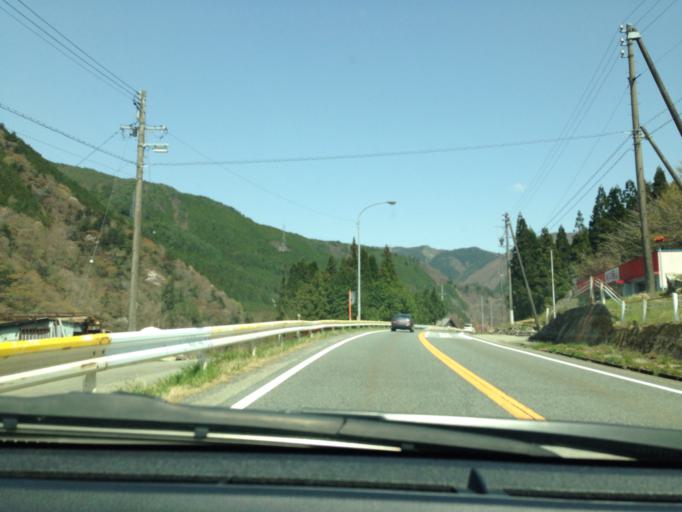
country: JP
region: Gifu
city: Takayama
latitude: 35.9588
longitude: 137.2605
